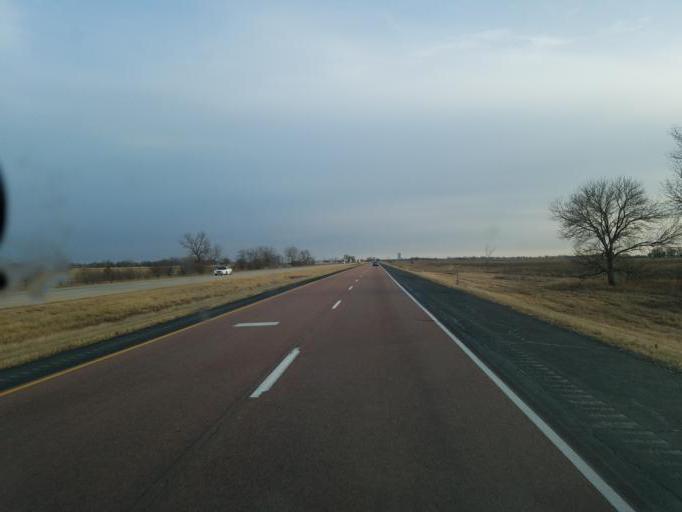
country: US
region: Iowa
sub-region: Monona County
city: Onawa
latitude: 42.0193
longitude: -96.1264
